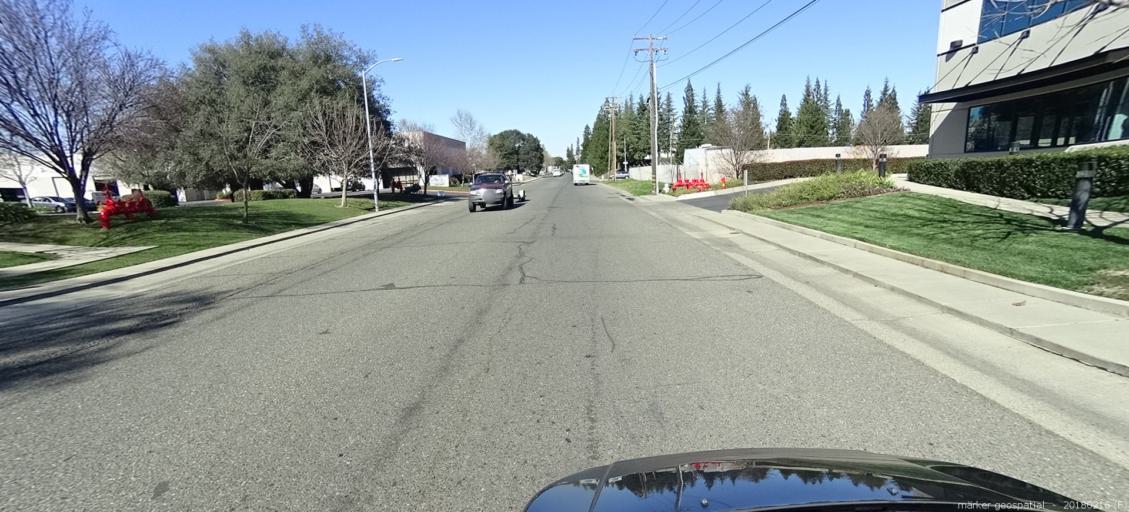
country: US
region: California
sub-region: Sacramento County
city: Gold River
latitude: 38.6151
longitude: -121.2599
